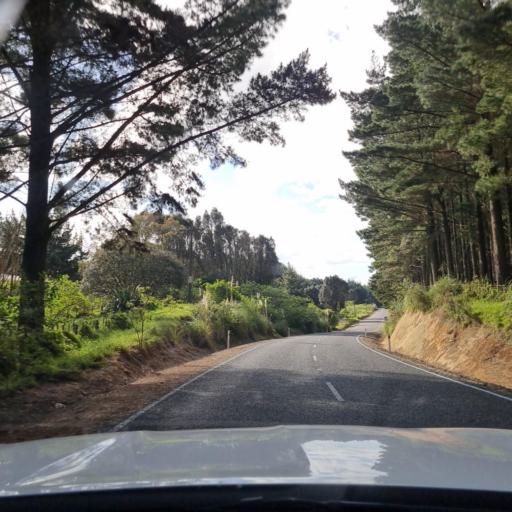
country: NZ
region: Northland
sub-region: Kaipara District
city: Dargaville
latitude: -36.2417
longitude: 174.0461
